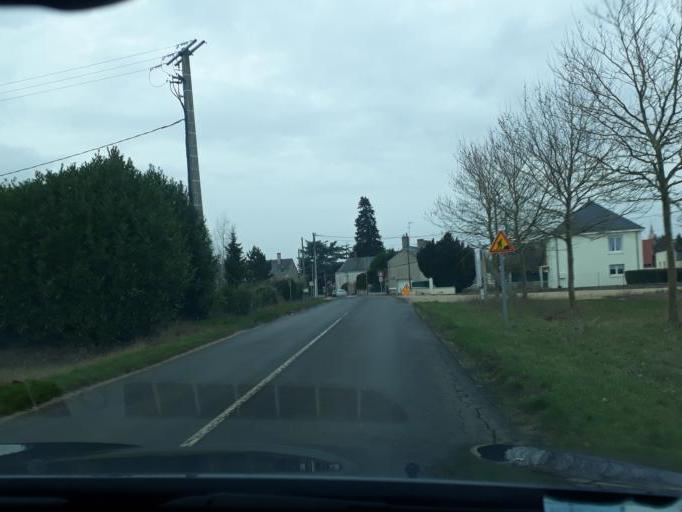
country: FR
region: Centre
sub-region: Departement du Loiret
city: Tavers
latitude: 47.7937
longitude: 1.5302
